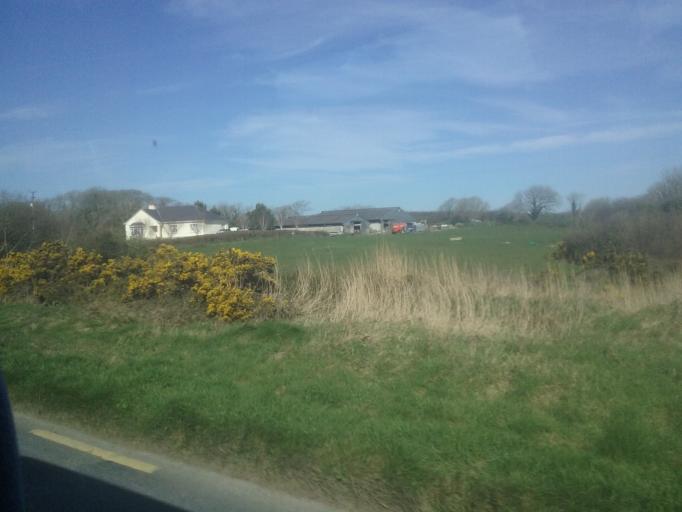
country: IE
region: Munster
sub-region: An Clar
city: Kilrush
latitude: 52.6150
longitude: -9.4513
